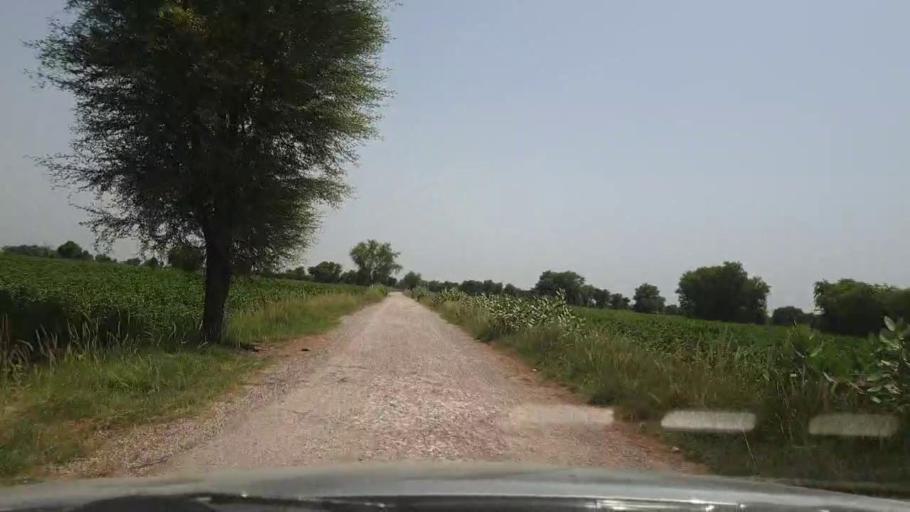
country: PK
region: Sindh
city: Pano Aqil
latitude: 27.7971
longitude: 69.2429
